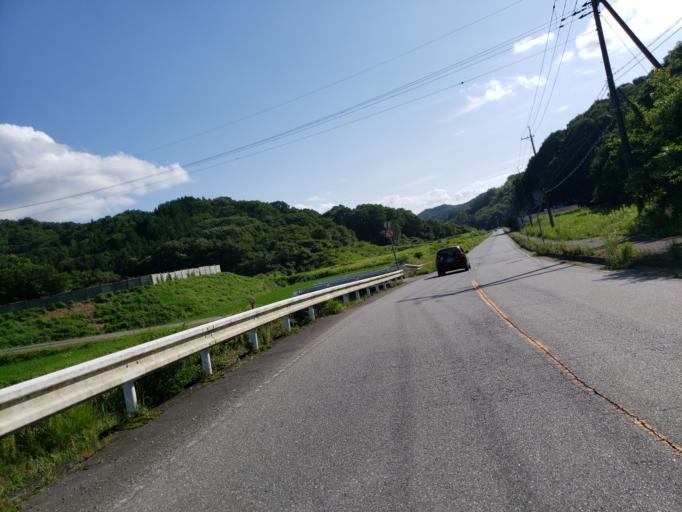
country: JP
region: Hyogo
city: Kakogawacho-honmachi
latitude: 34.8876
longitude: 134.8069
